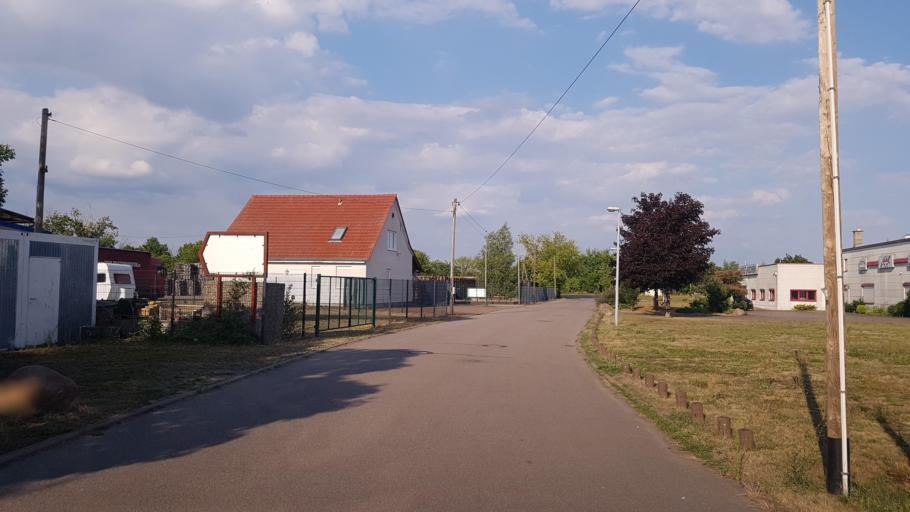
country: DE
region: Saxony
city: Beilrode
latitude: 51.5849
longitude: 13.0719
